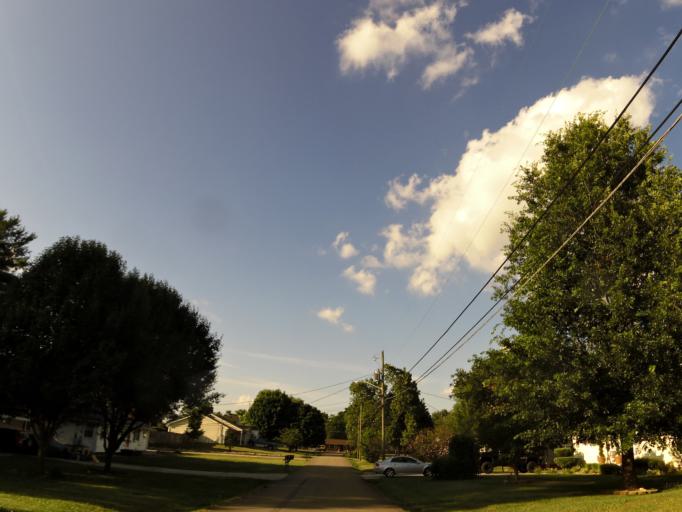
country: US
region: Tennessee
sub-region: Knox County
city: Knoxville
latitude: 36.0006
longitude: -83.9784
